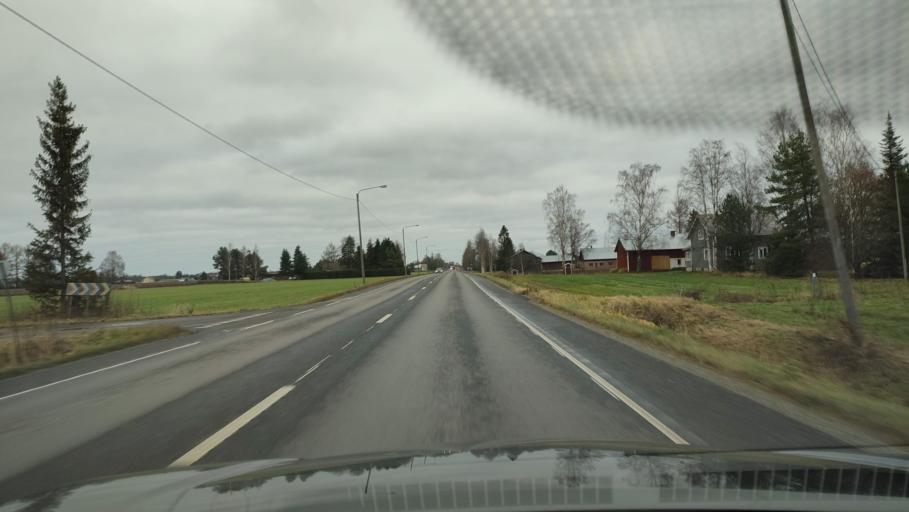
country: FI
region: Southern Ostrobothnia
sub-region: Seinaejoki
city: Ilmajoki
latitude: 62.6982
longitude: 22.5095
